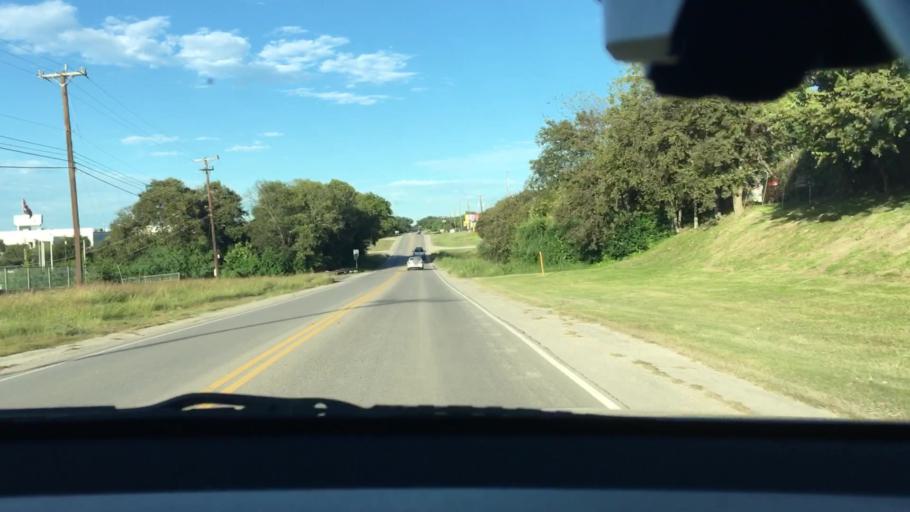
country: US
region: Texas
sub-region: Bexar County
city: Windcrest
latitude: 29.5444
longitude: -98.3650
